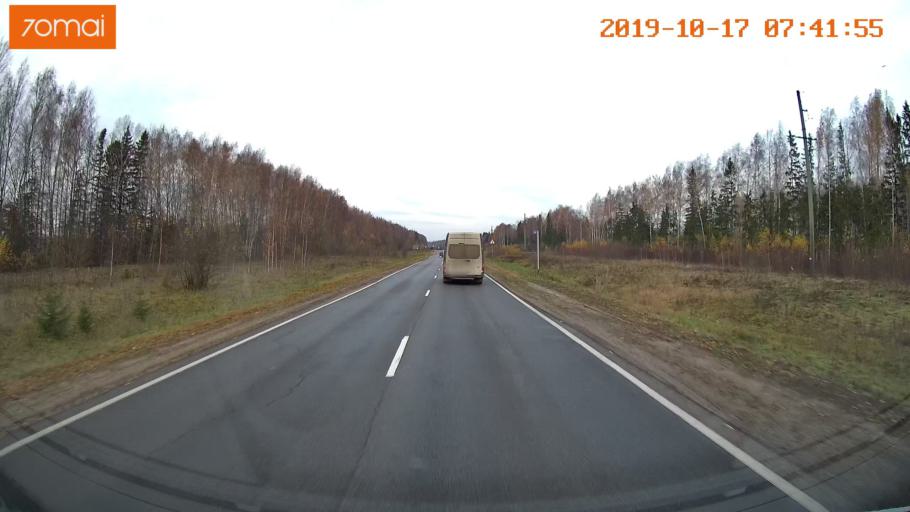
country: RU
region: Vladimir
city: Yur'yev-Pol'skiy
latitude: 56.4836
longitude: 39.7984
